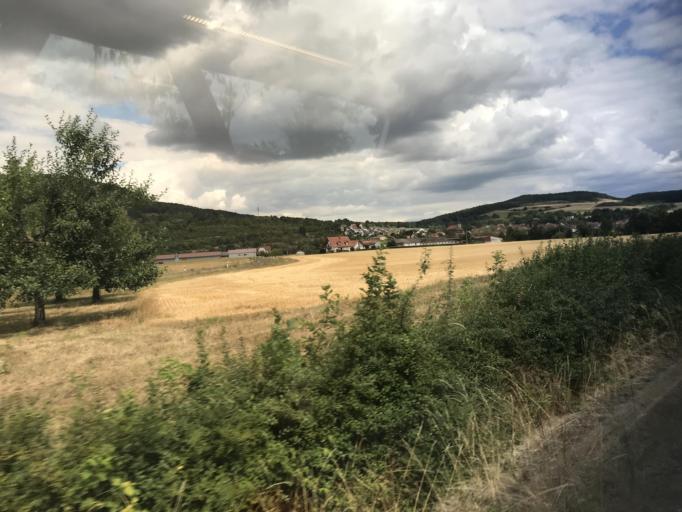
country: DE
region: Bavaria
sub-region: Regierungsbezirk Unterfranken
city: Elfershausen
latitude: 50.1389
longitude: 9.9556
